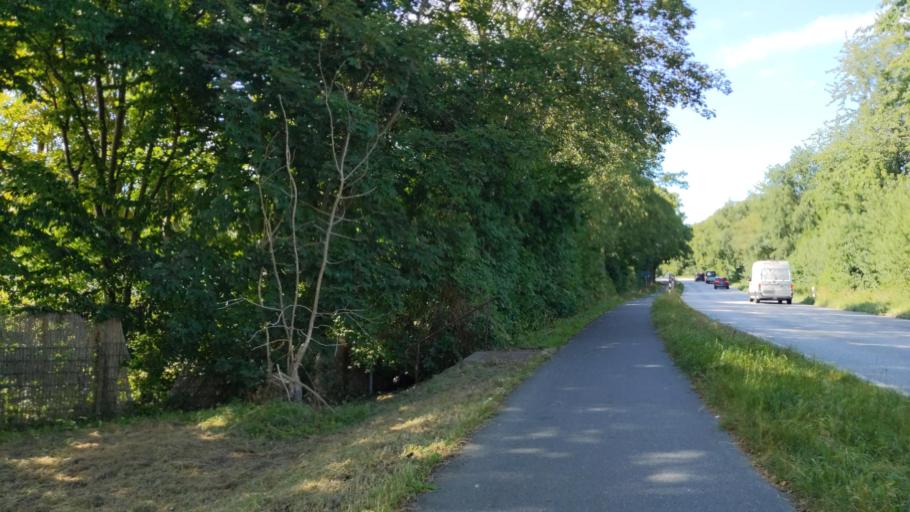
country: DE
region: Schleswig-Holstein
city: Dornick
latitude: 54.1537
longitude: 10.3854
